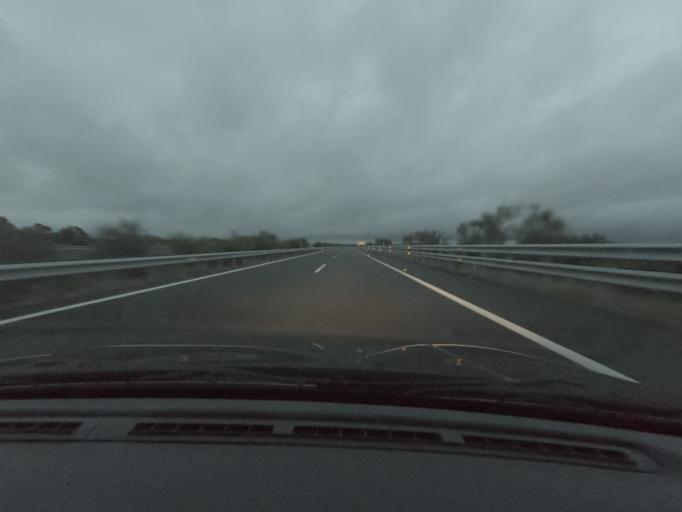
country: ES
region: Extremadura
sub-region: Provincia de Caceres
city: Aldea del Cano
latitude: 39.2624
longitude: -6.3158
